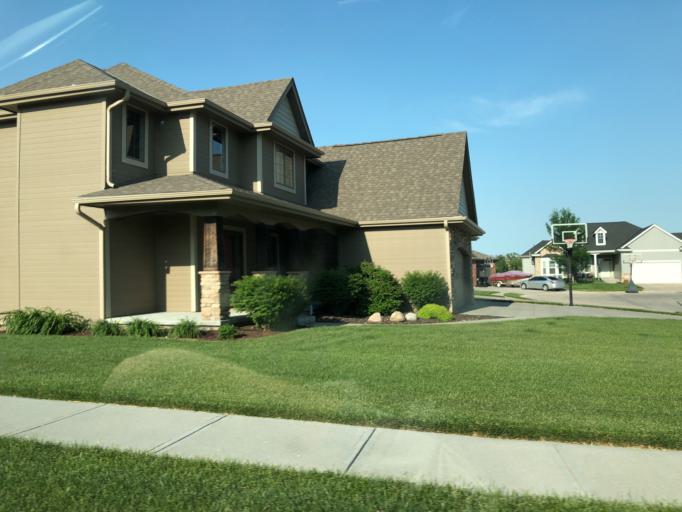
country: US
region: Nebraska
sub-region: Douglas County
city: Elkhorn
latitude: 41.2789
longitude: -96.1883
